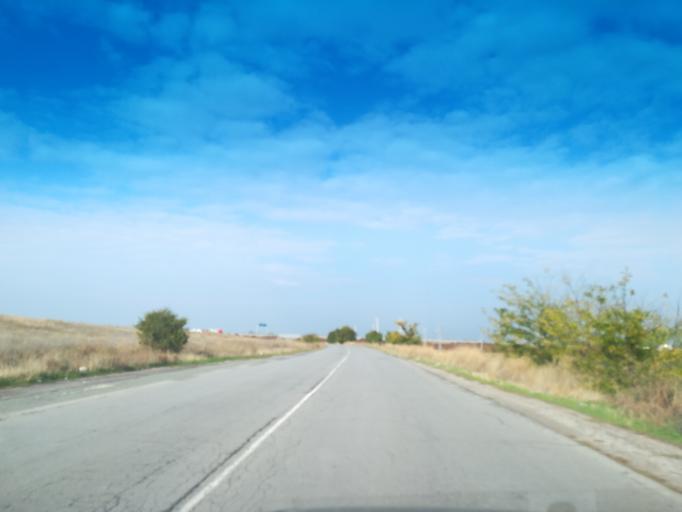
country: BG
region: Stara Zagora
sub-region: Obshtina Chirpan
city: Chirpan
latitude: 42.2061
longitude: 25.3073
